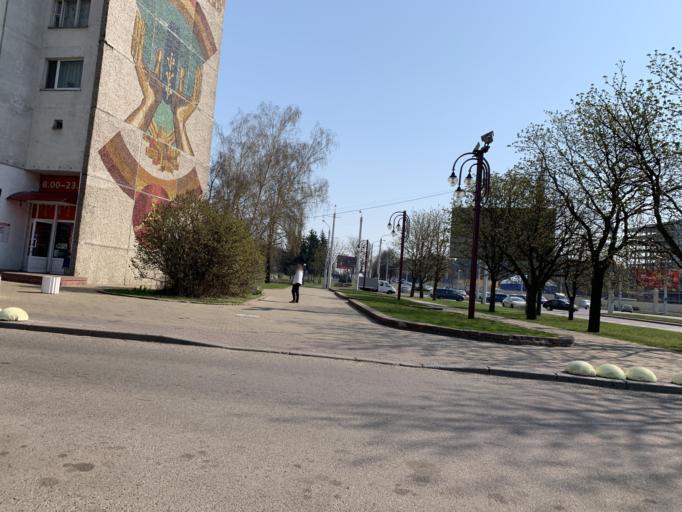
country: BY
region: Minsk
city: Borovlyany
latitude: 53.9358
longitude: 27.6544
